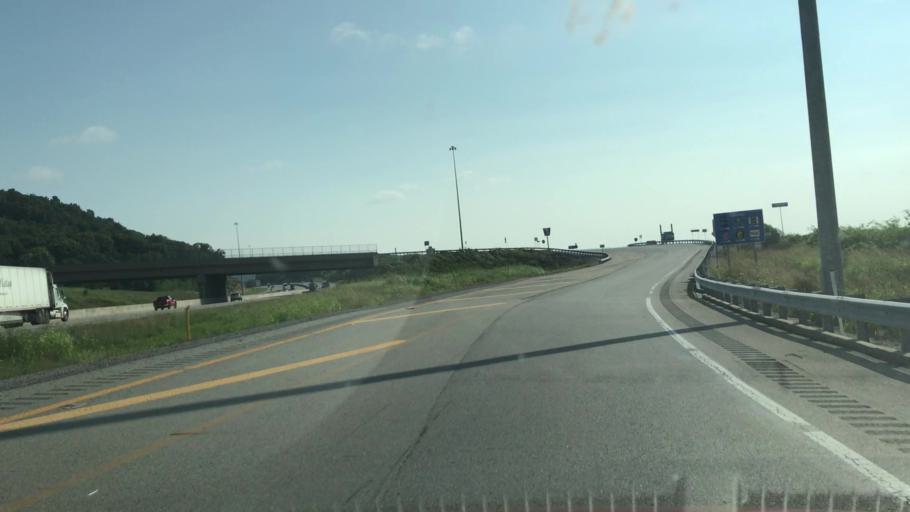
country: US
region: Kentucky
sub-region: Barren County
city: Cave City
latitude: 37.1341
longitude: -85.9793
